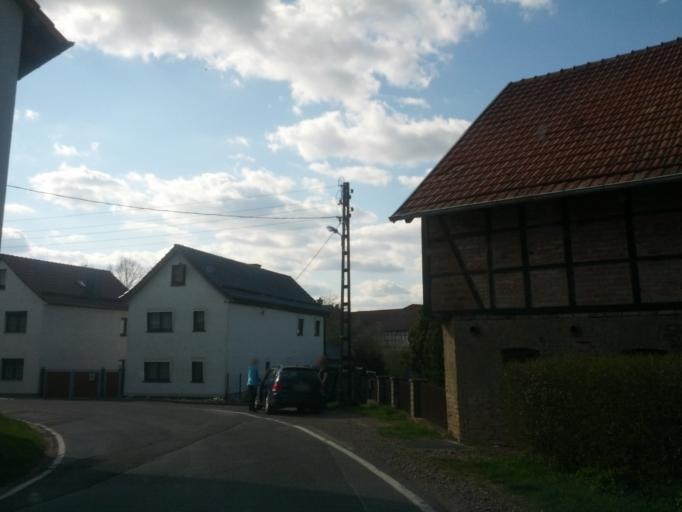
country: DE
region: Thuringia
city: Seebach
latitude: 50.9733
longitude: 10.4503
